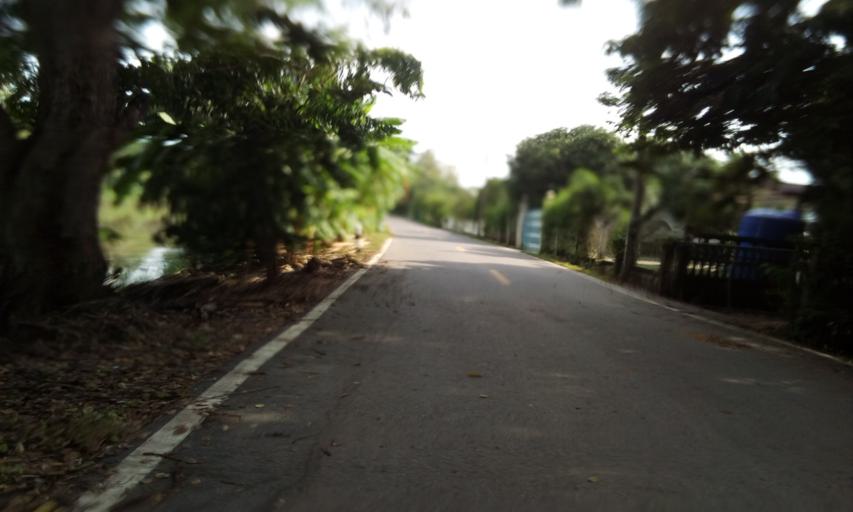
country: TH
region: Pathum Thani
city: Nong Suea
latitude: 14.1199
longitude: 100.8235
